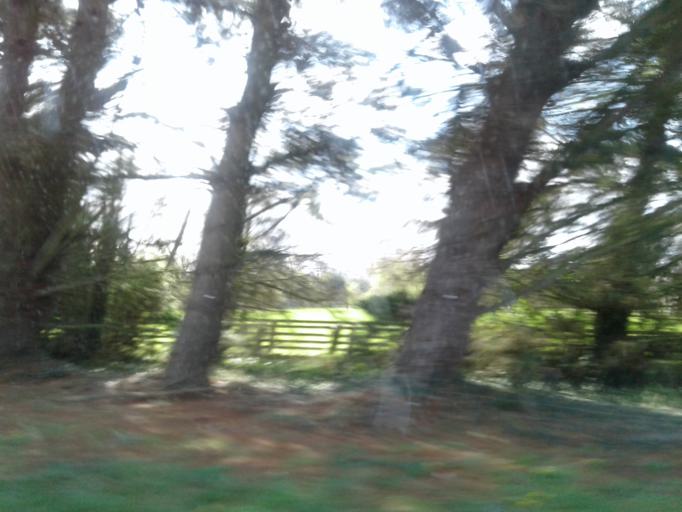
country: IE
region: Leinster
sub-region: Fingal County
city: Swords
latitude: 53.4746
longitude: -6.2634
